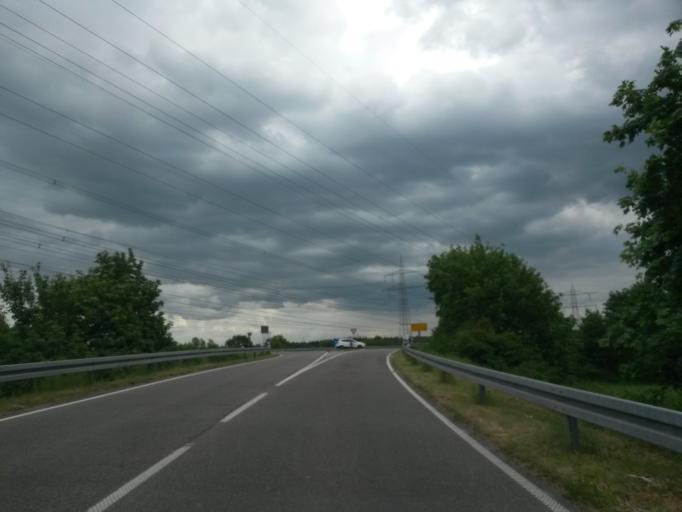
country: DE
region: Baden-Wuerttemberg
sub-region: Karlsruhe Region
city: Waghausel
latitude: 49.2505
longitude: 8.4962
